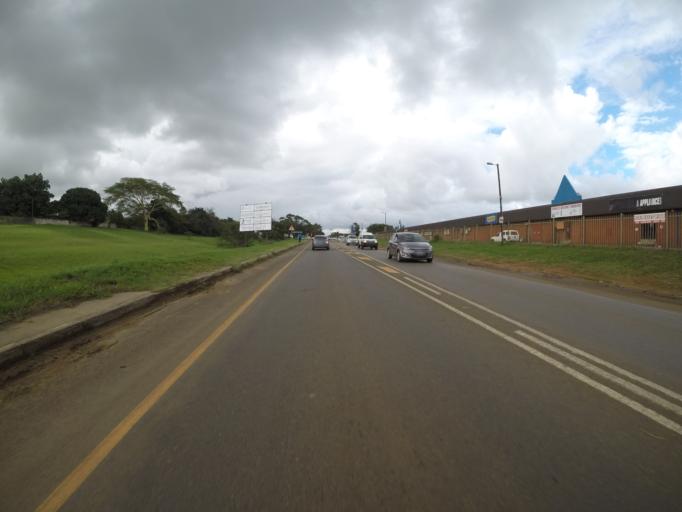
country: ZA
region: KwaZulu-Natal
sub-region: uMkhanyakude District Municipality
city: Mtubatuba
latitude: -28.4160
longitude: 32.1840
